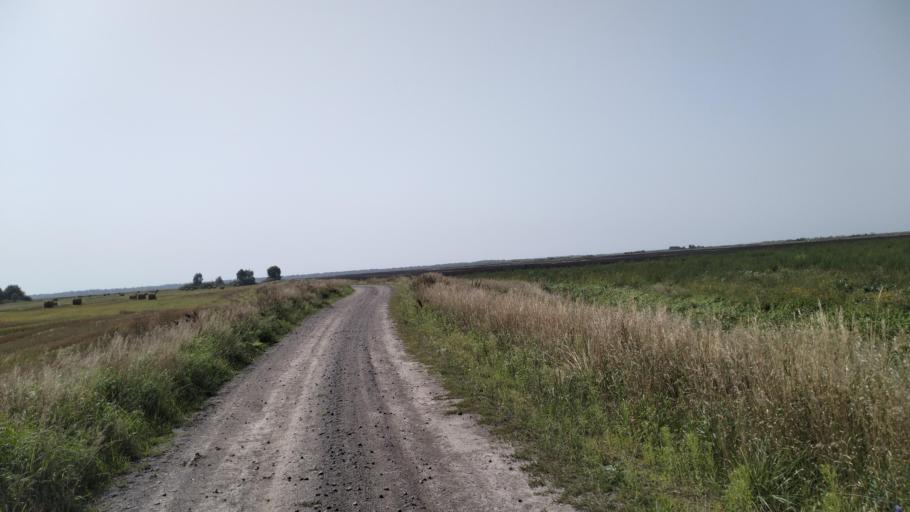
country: BY
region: Brest
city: Davyd-Haradok
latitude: 52.0025
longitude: 27.1654
